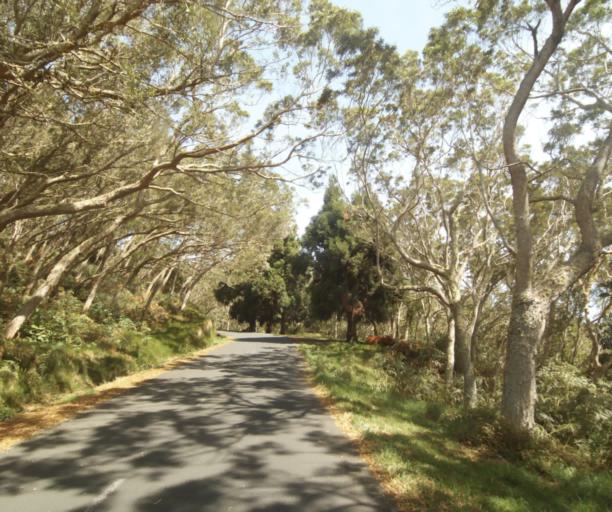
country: RE
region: Reunion
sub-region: Reunion
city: Trois-Bassins
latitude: -21.0568
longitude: 55.3636
